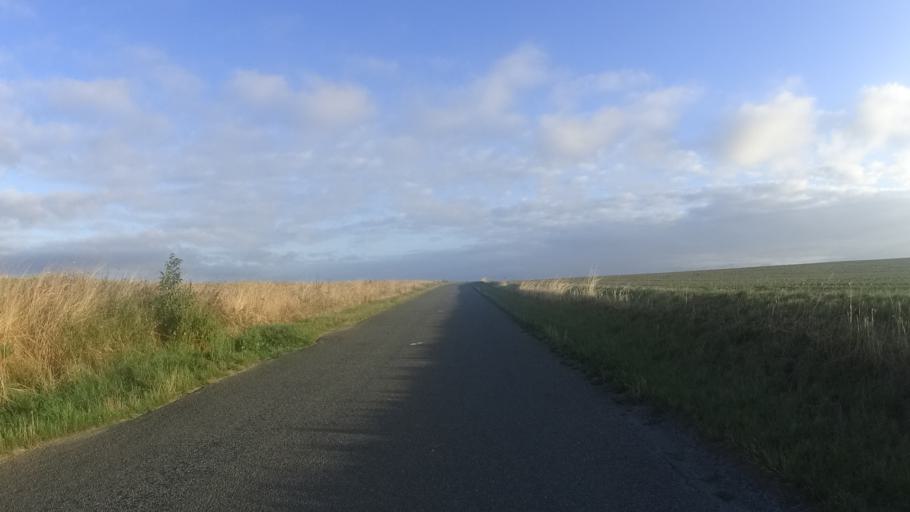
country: FR
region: Picardie
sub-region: Departement de l'Oise
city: Chamant
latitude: 49.1851
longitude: 2.6724
